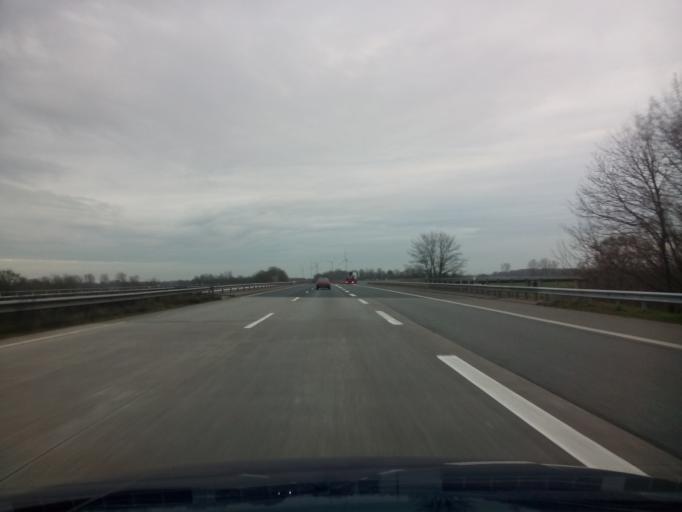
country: DE
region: Lower Saxony
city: Loxstedt
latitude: 53.4655
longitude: 8.6021
